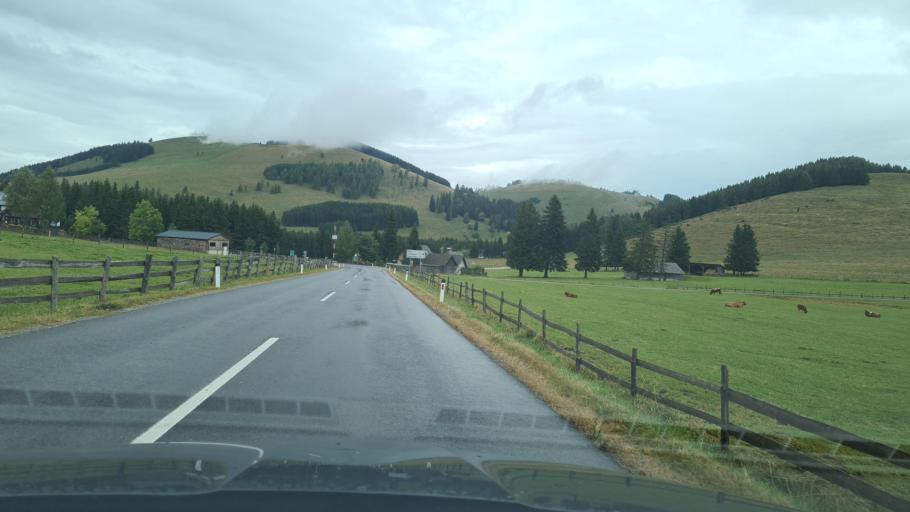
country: AT
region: Styria
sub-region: Politischer Bezirk Weiz
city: Passail
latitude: 47.3407
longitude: 15.4774
